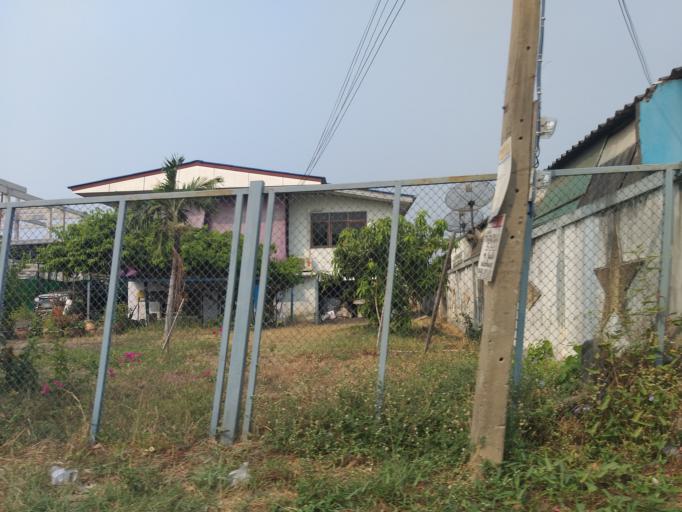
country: TH
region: Phra Nakhon Si Ayutthaya
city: Ban Bang Kadi Pathum Thani
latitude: 14.0180
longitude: 100.5684
